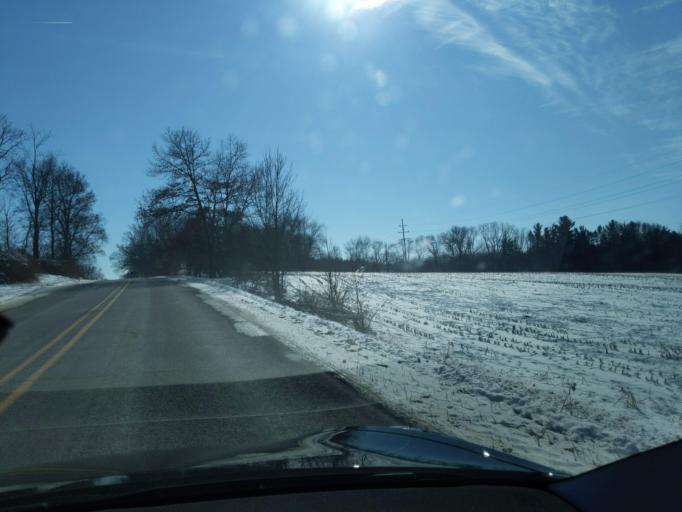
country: US
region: Michigan
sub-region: Livingston County
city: Fowlerville
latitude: 42.5630
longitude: -84.0723
